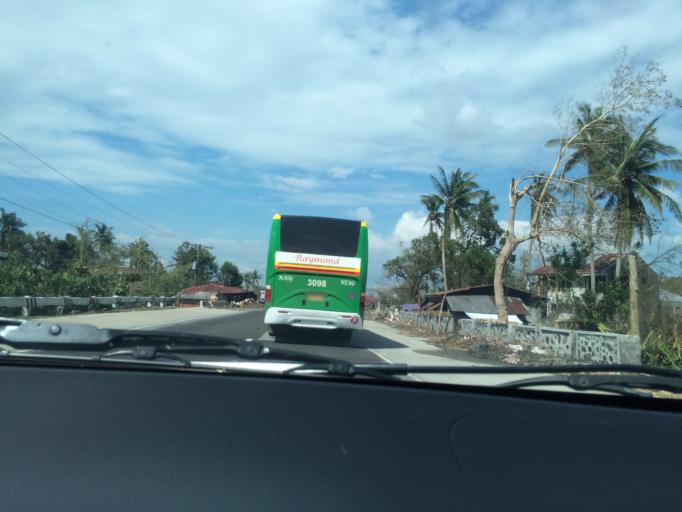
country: PH
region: Bicol
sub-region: Province of Albay
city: Iraya
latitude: 13.2613
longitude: 123.4978
